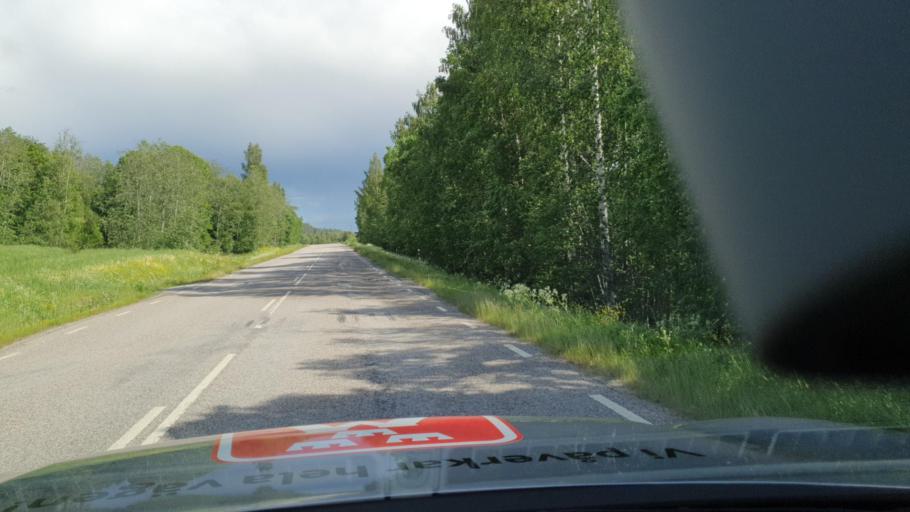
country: SE
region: Vaesternorrland
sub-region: OErnskoeldsviks Kommun
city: Bjasta
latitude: 63.2599
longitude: 18.3422
